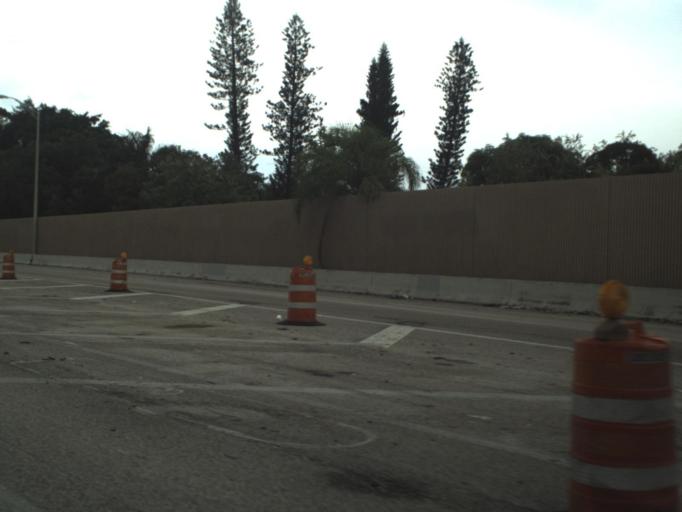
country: US
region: Florida
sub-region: Broward County
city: Hollywood
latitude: 26.0290
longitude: -80.1653
